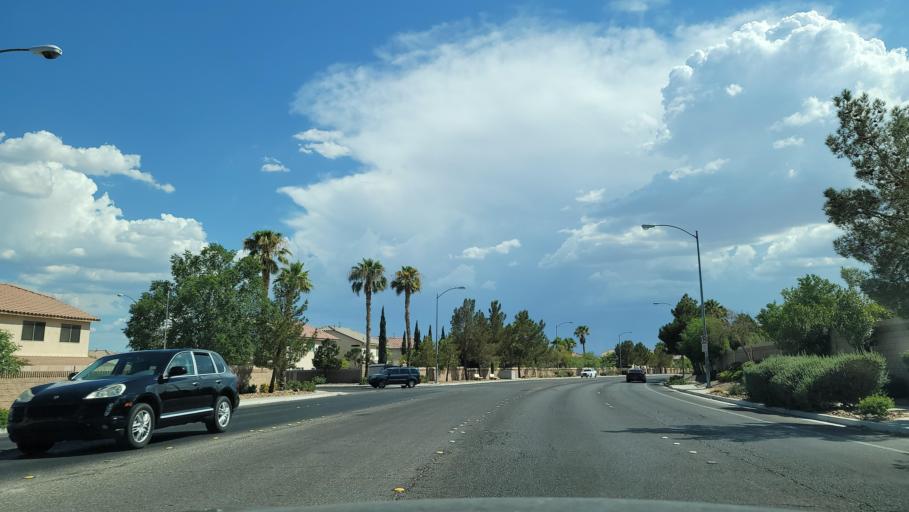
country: US
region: Nevada
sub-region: Clark County
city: Spring Valley
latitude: 36.1329
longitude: -115.2689
